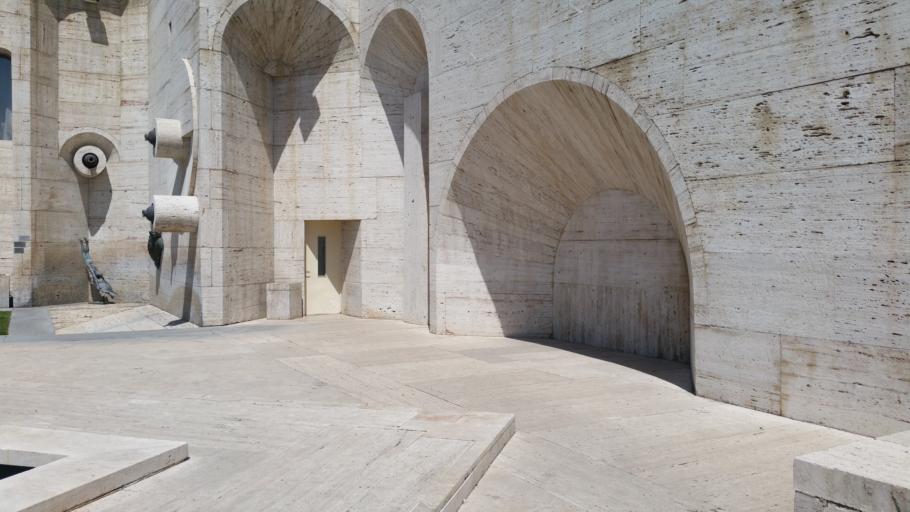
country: AM
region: Yerevan
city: Yerevan
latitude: 40.1922
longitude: 44.5159
